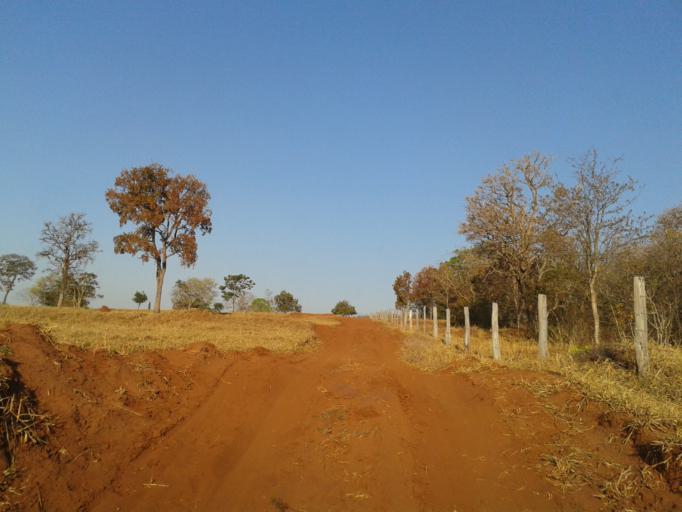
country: BR
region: Minas Gerais
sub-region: Campina Verde
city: Campina Verde
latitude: -19.2613
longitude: -49.6134
